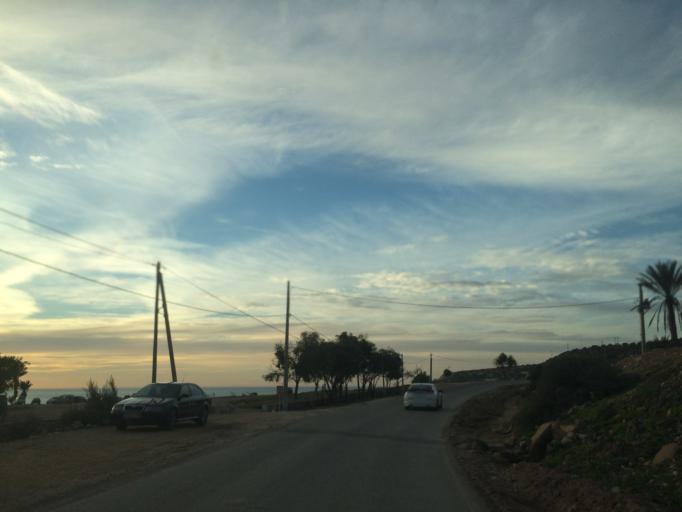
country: MA
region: Souss-Massa-Draa
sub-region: Agadir-Ida-ou-Tnan
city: Taghazout
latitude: 30.5465
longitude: -9.7248
